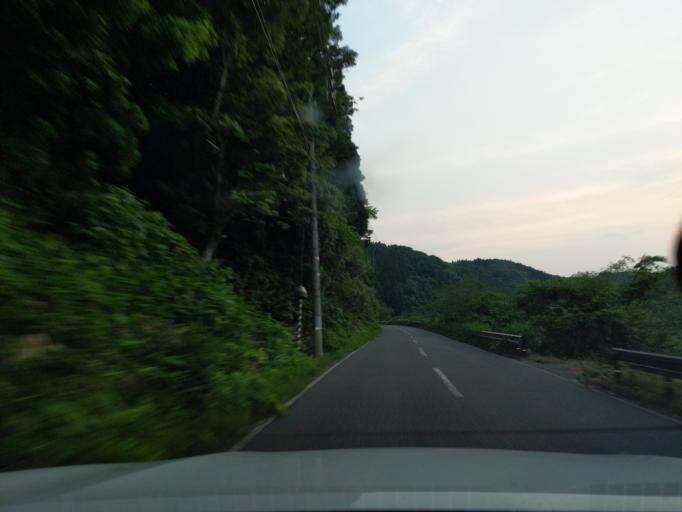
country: JP
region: Niigata
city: Kashiwazaki
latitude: 37.4526
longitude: 138.6275
